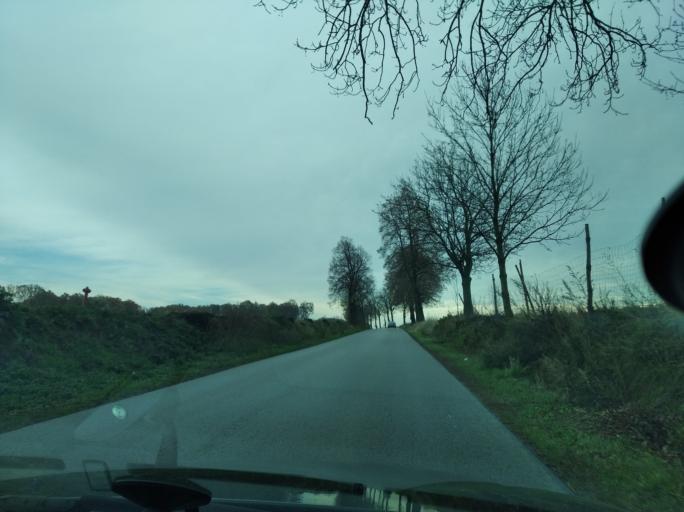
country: PL
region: Subcarpathian Voivodeship
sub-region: Powiat lancucki
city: Wysoka
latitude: 50.0298
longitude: 22.2427
